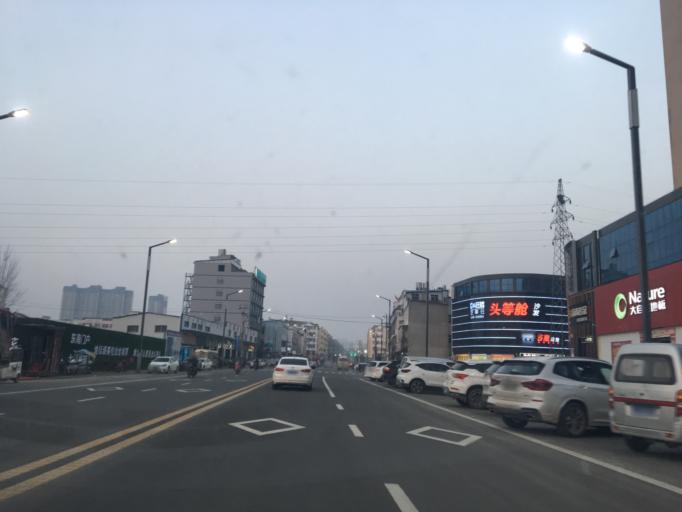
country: CN
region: Hubei
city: Gulou
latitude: 31.1674
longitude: 115.0296
